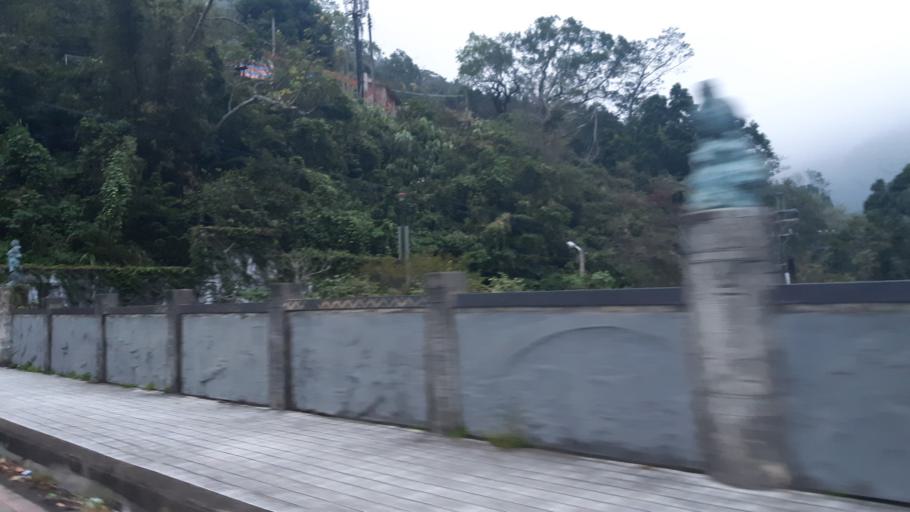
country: TW
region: Taiwan
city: Daxi
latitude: 24.6878
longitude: 121.2182
